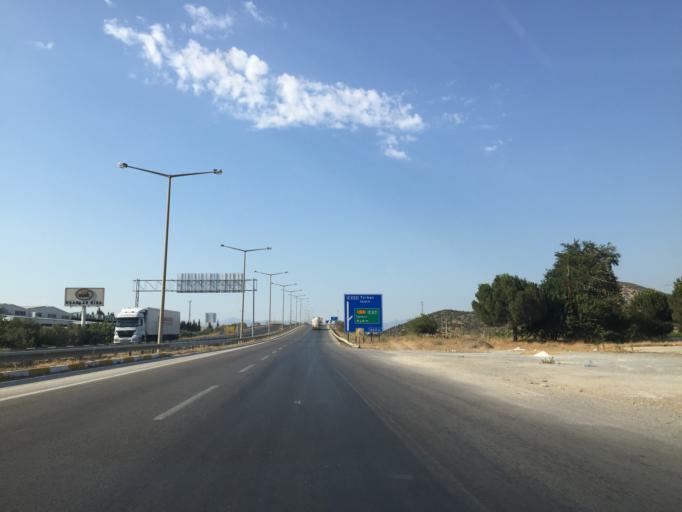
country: TR
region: Izmir
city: Belevi
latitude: 38.0217
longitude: 27.4413
